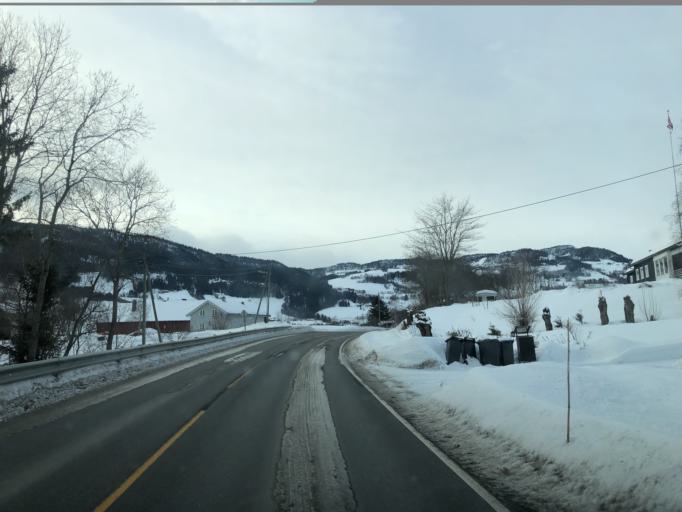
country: NO
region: Oppland
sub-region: Gausdal
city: Segalstad bru
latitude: 61.2611
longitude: 10.1607
